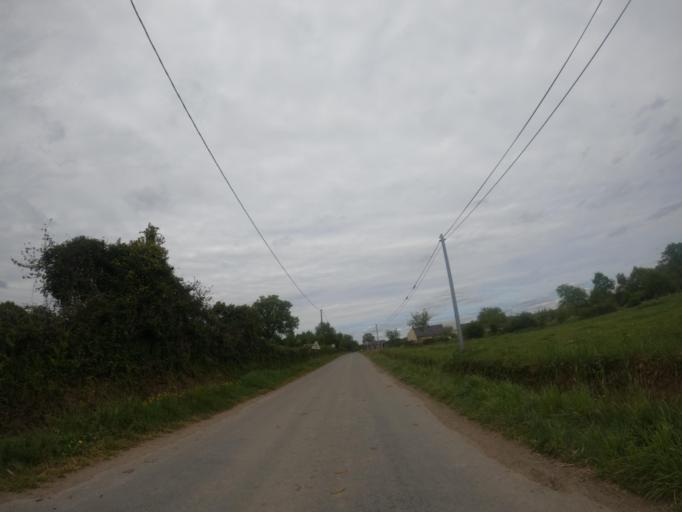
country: FR
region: Pays de la Loire
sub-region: Departement de la Loire-Atlantique
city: Saint-Aubin-des-Chateaux
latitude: 47.7351
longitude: -1.4440
